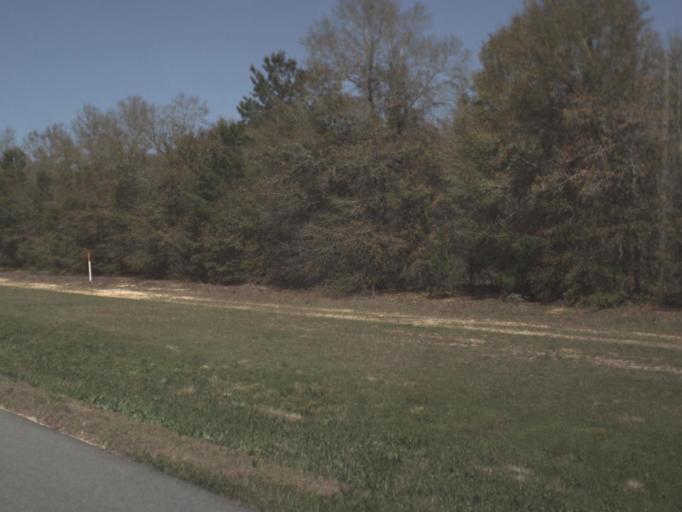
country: US
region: Florida
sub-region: Okaloosa County
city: Crestview
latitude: 30.7387
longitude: -86.3661
